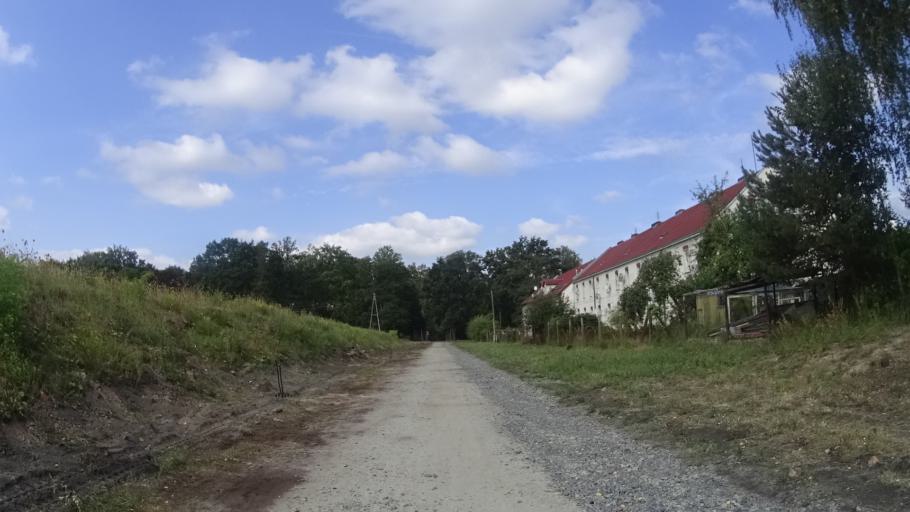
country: PL
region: Lubusz
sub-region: Powiat zarski
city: Leknica
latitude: 51.5361
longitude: 14.7390
